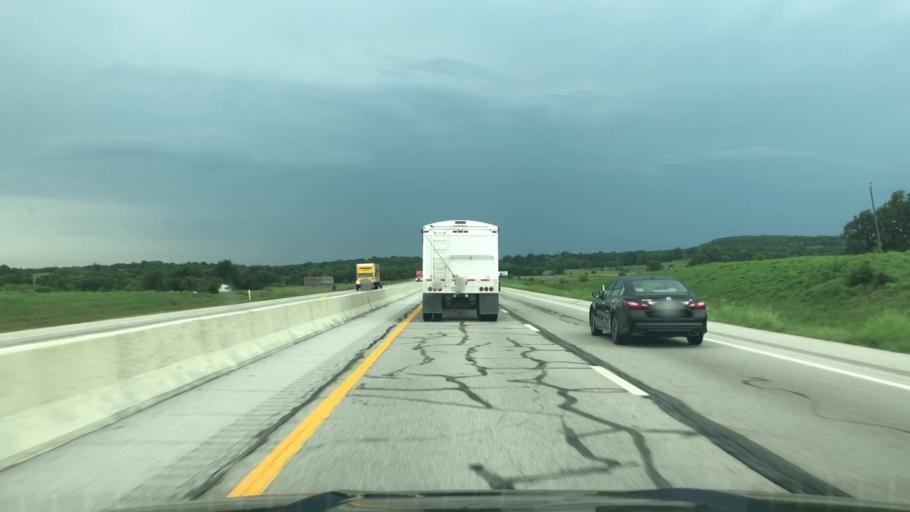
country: US
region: Oklahoma
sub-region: Rogers County
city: Bushyhead
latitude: 36.4054
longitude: -95.4116
